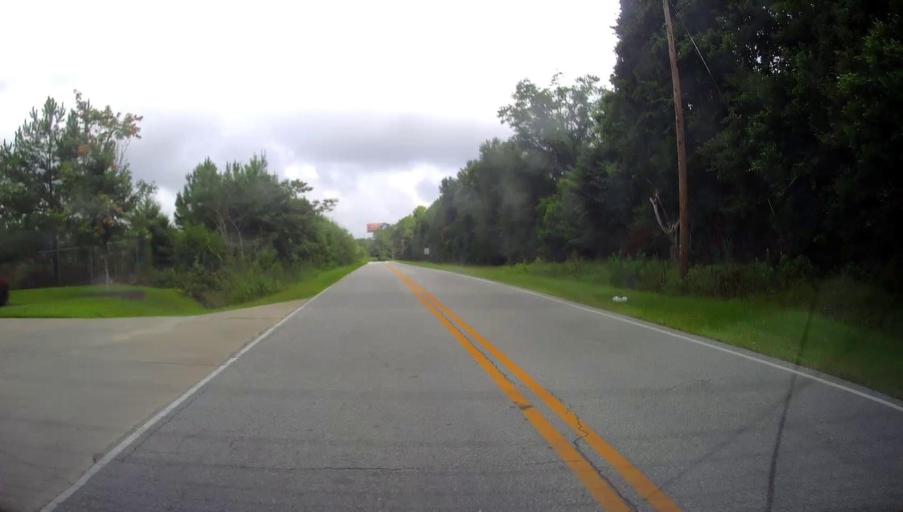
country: US
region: Georgia
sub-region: Bibb County
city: West Point
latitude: 32.8197
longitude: -83.7268
